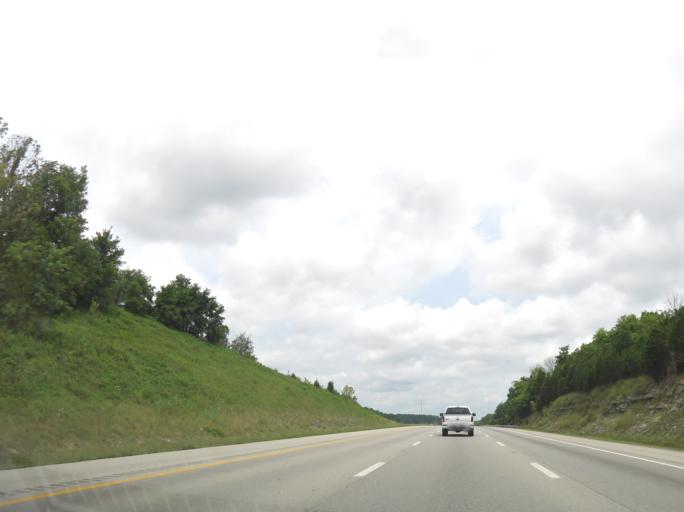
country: US
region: Kentucky
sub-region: Grant County
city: Williamstown
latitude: 38.4600
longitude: -84.5753
